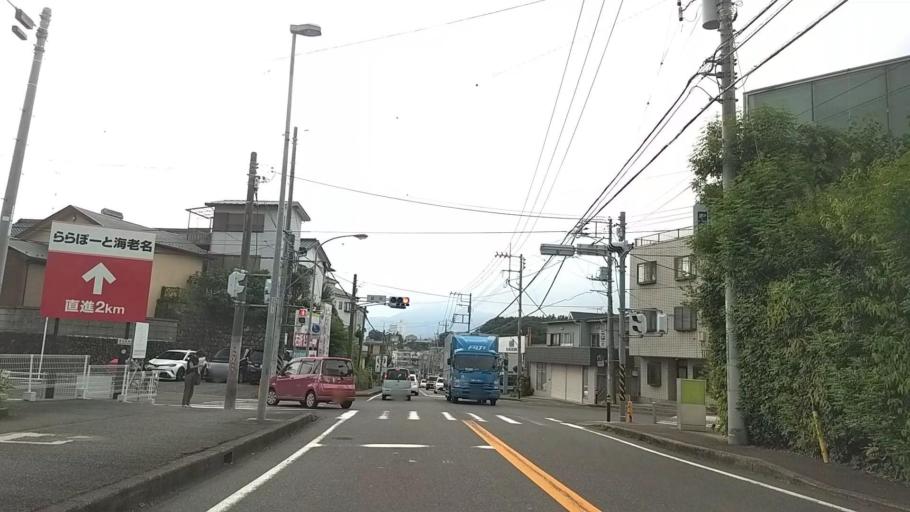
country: JP
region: Kanagawa
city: Zama
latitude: 35.4535
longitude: 139.4069
